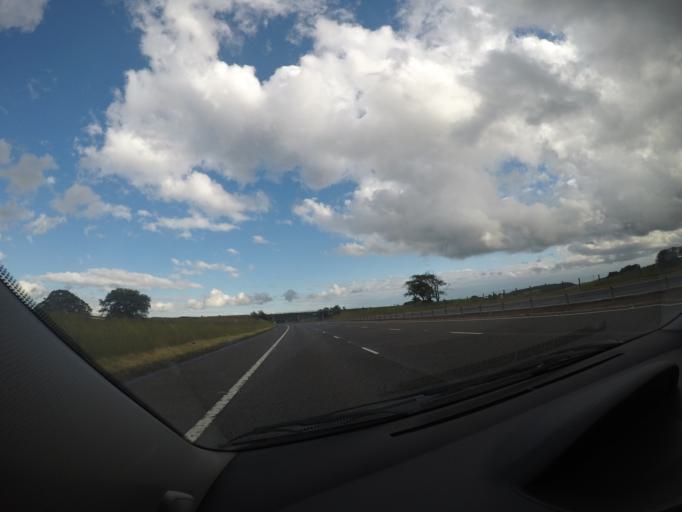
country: GB
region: Scotland
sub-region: Dumfries and Galloway
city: Lockerbie
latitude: 55.1056
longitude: -3.3511
